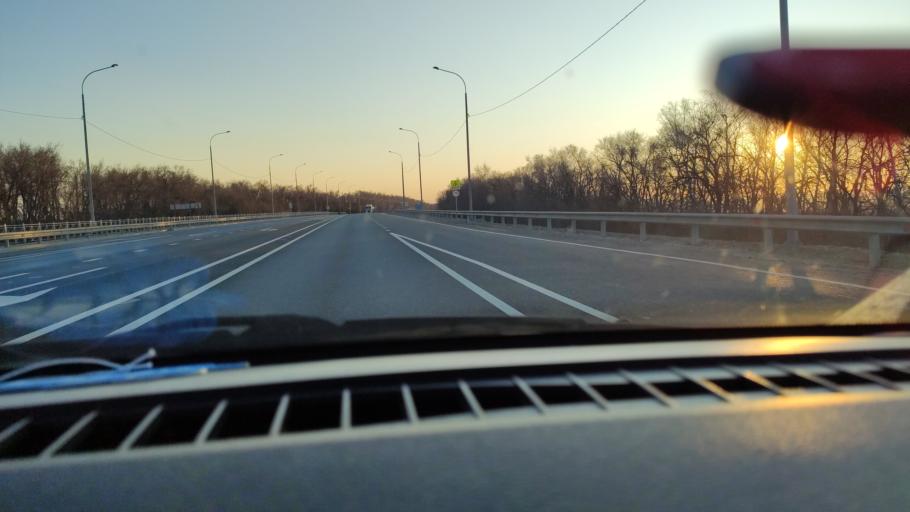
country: RU
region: Saratov
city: Yelshanka
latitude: 51.8949
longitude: 46.5299
